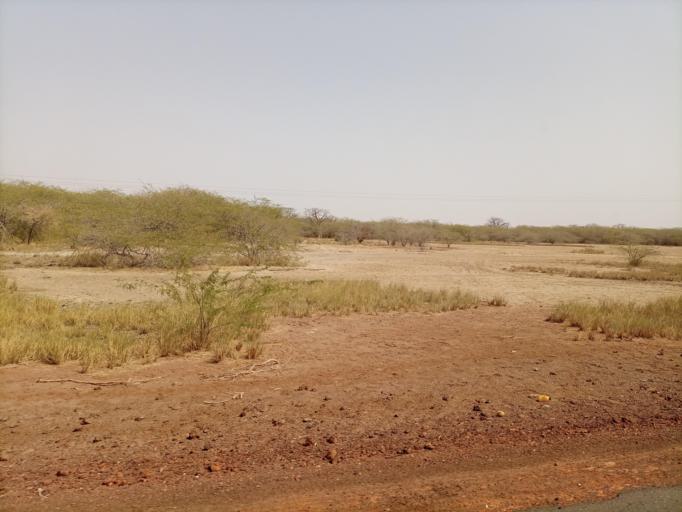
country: SN
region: Fatick
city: Foundiougne
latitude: 14.1795
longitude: -16.4575
